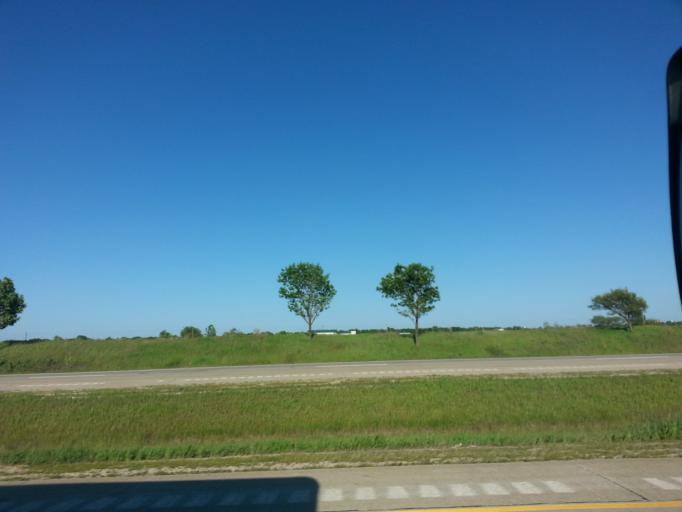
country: US
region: Illinois
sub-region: Woodford County
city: El Paso
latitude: 40.7564
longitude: -89.0346
